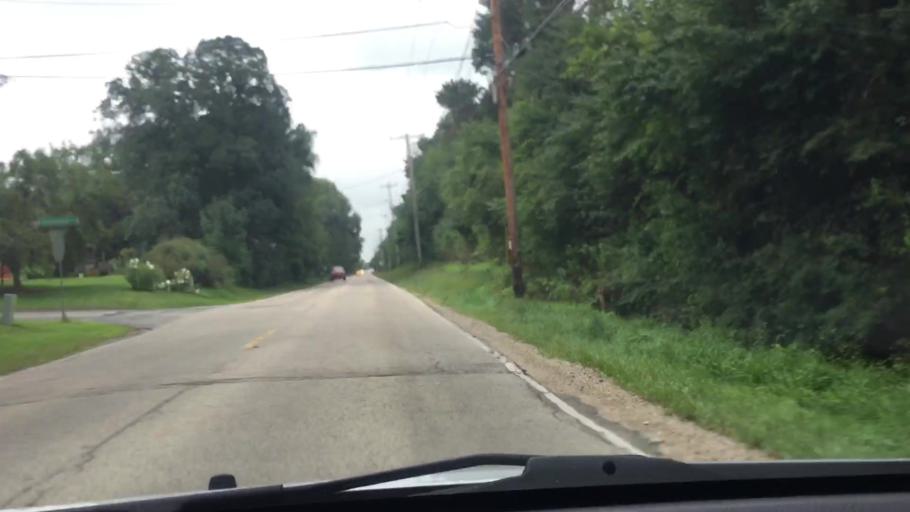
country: US
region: Wisconsin
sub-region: Waukesha County
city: Delafield
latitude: 43.0531
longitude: -88.4424
